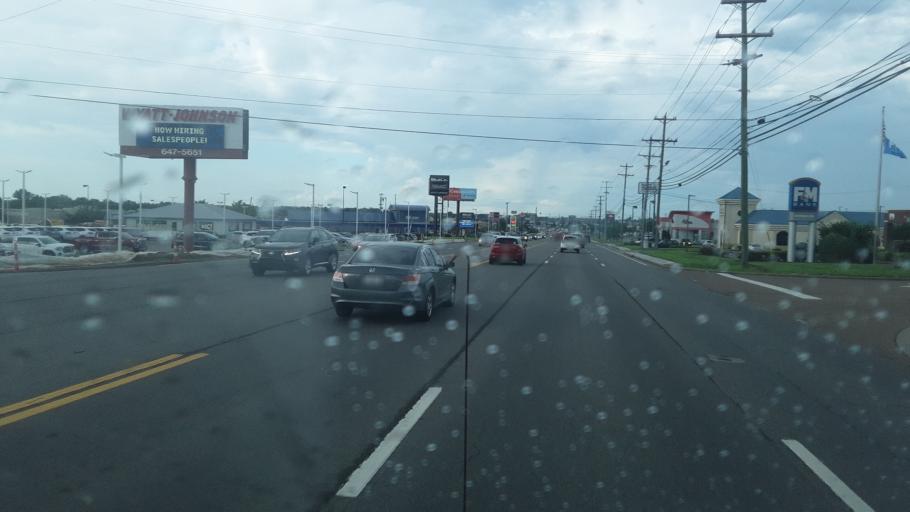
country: US
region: Tennessee
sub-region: Montgomery County
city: Clarksville
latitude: 36.5796
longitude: -87.2991
